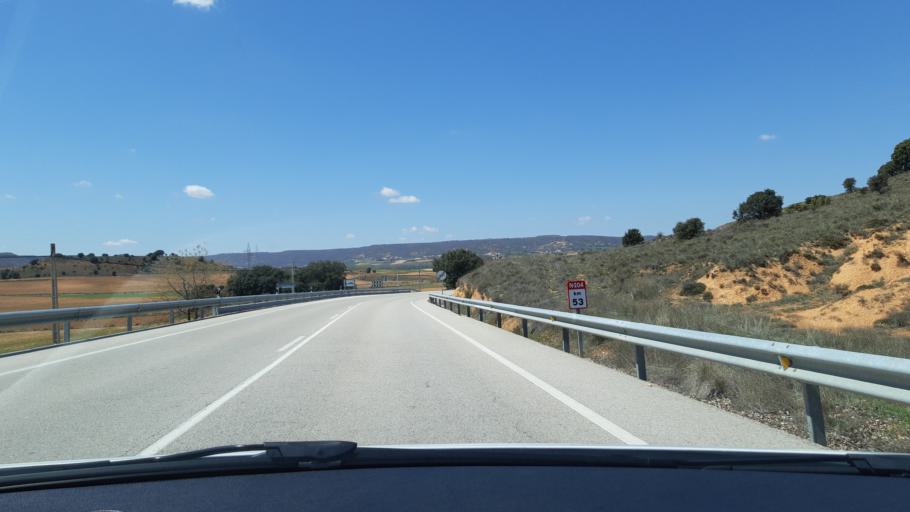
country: ES
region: Castille-La Mancha
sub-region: Provincia de Guadalajara
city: Masegoso de Tajuna
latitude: 40.8117
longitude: -2.6818
